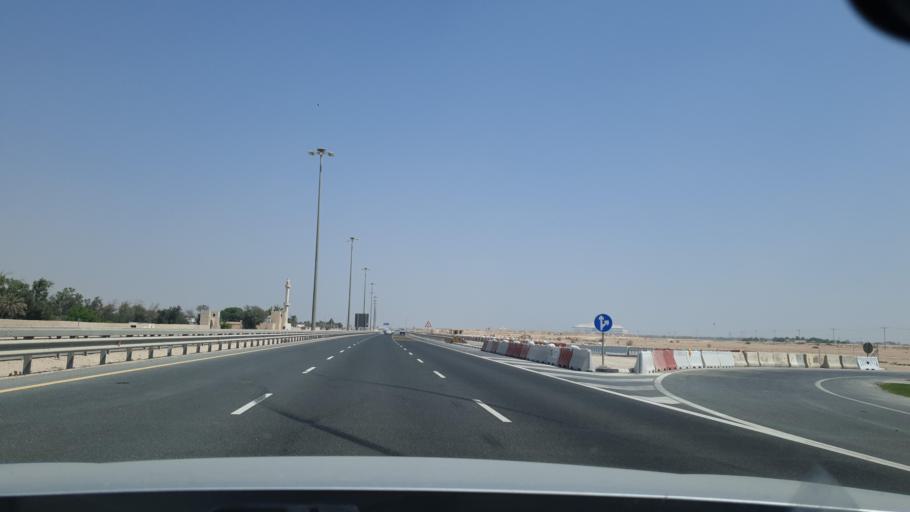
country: QA
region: Al Khawr
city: Al Khawr
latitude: 25.6459
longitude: 51.4420
